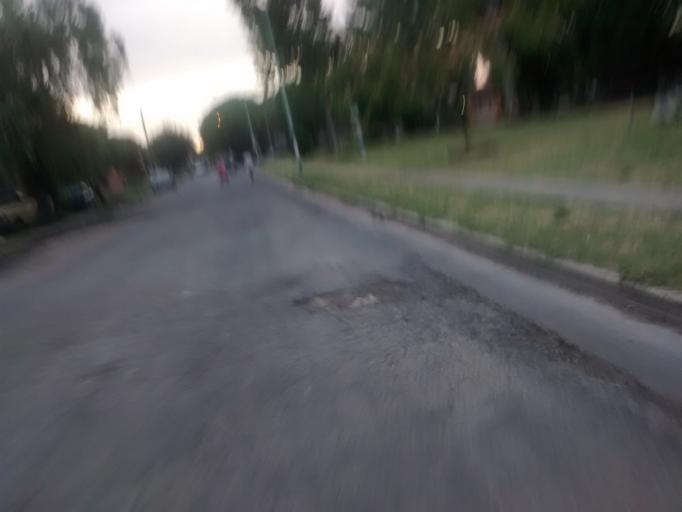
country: AR
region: Buenos Aires
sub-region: Partido de La Plata
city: La Plata
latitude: -34.9444
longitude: -57.9174
